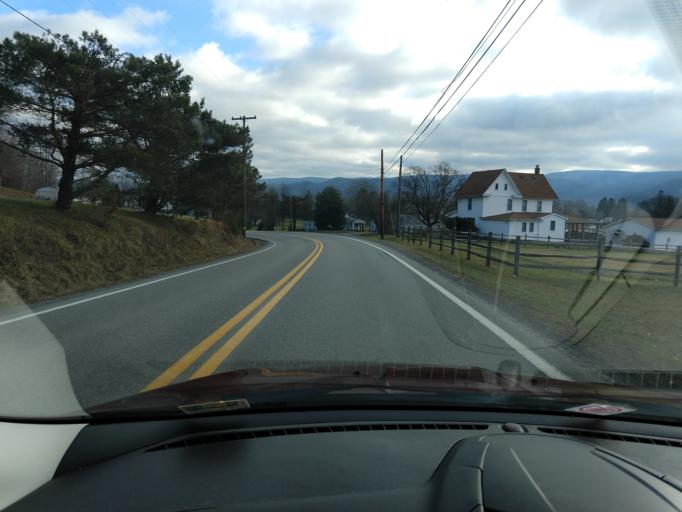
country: US
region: West Virginia
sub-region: Randolph County
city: Elkins
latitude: 38.7724
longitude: -79.9252
